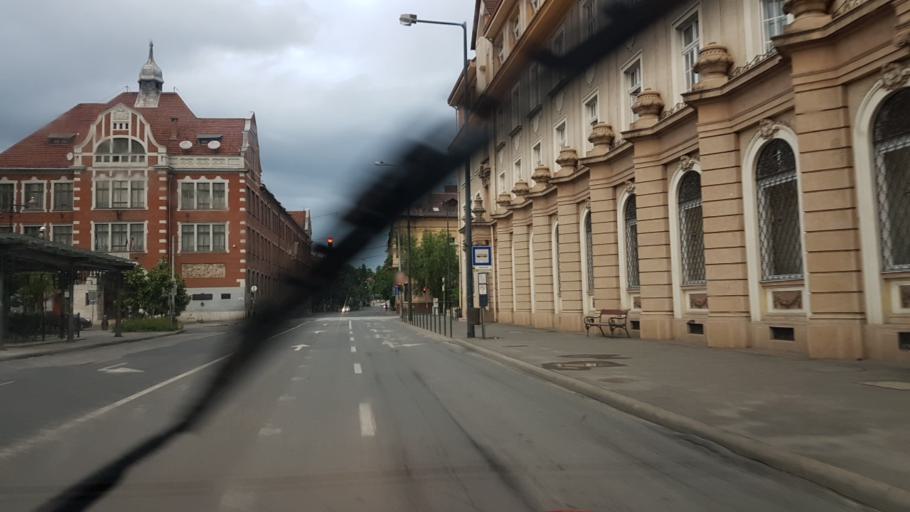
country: HU
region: Borsod-Abauj-Zemplen
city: Miskolc
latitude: 48.1047
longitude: 20.7854
